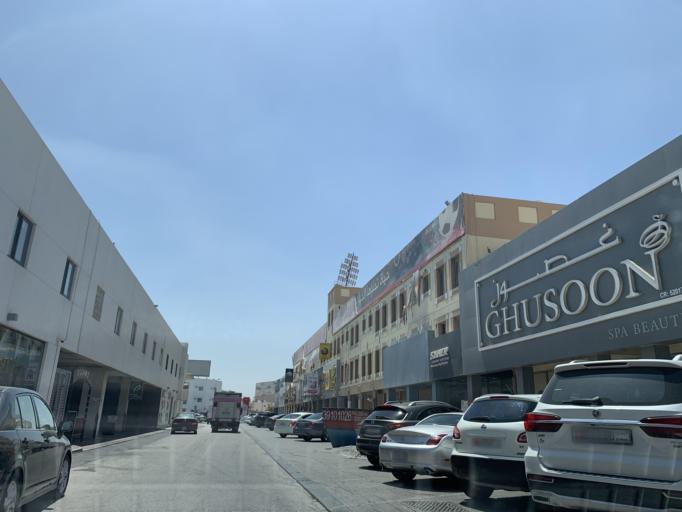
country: BH
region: Muharraq
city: Al Muharraq
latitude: 26.2583
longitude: 50.6285
